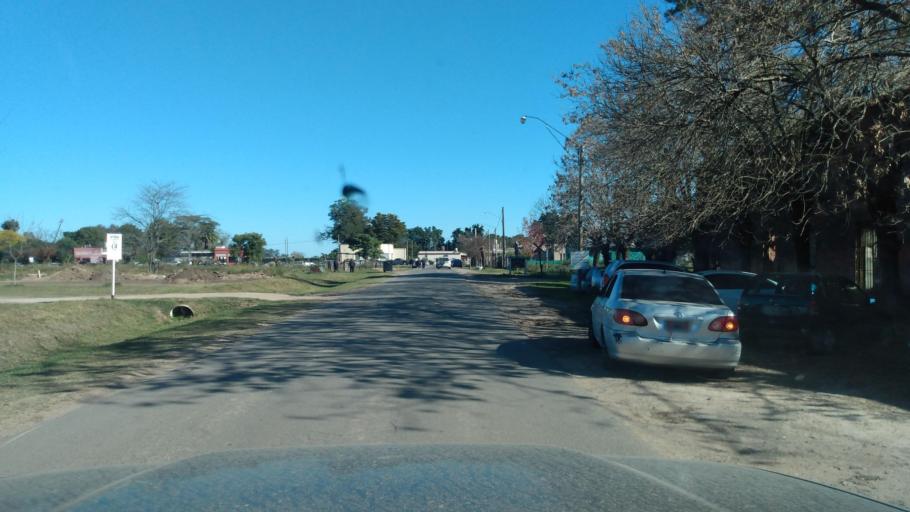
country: AR
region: Buenos Aires
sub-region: Partido de Lujan
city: Lujan
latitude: -34.4843
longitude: -59.2219
